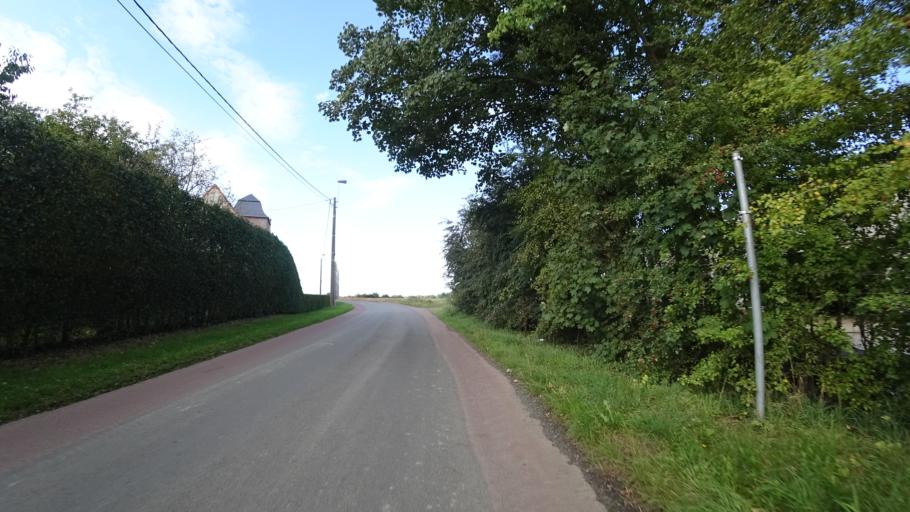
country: BE
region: Wallonia
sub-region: Province du Brabant Wallon
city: Chastre
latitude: 50.5832
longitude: 4.6011
